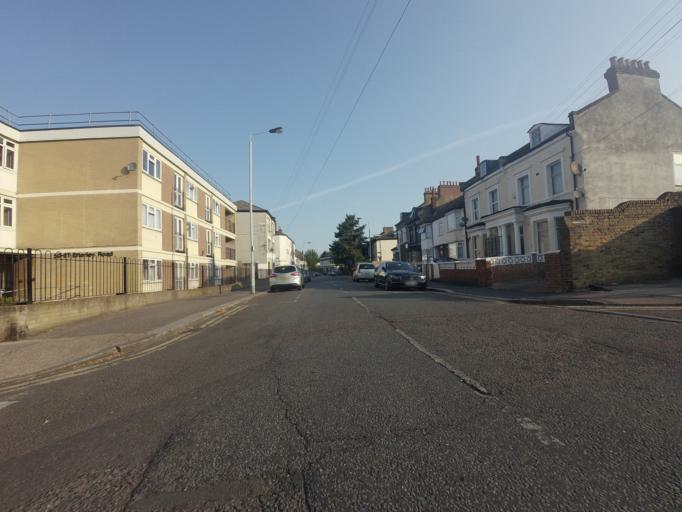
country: GB
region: England
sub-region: Greater London
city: Walthamstow
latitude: 51.5554
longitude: 0.0013
